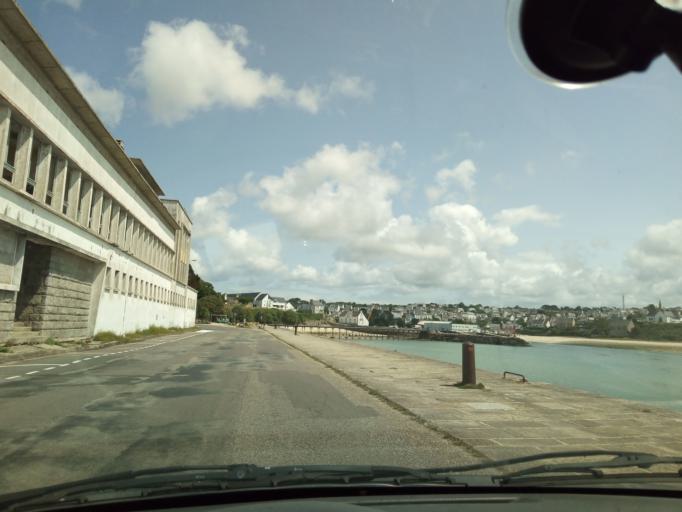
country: FR
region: Brittany
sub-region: Departement du Finistere
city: Audierne
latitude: 48.0152
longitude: -4.5389
